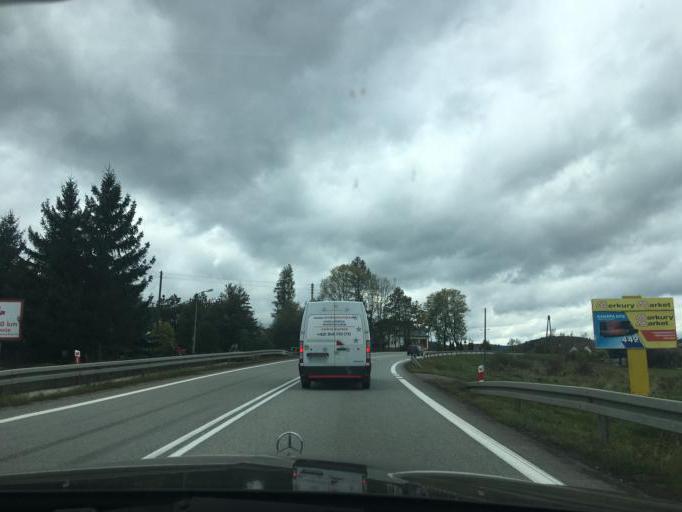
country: PL
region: Subcarpathian Voivodeship
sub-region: Powiat krosnienski
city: Jasliska
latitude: 49.4309
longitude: 21.6883
